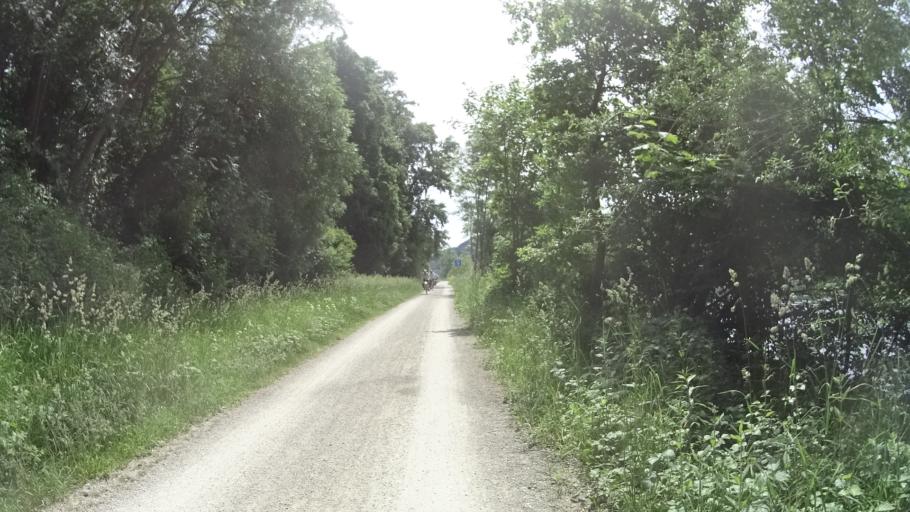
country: DE
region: Bavaria
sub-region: Lower Bavaria
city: Saal
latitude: 48.9093
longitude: 11.9400
